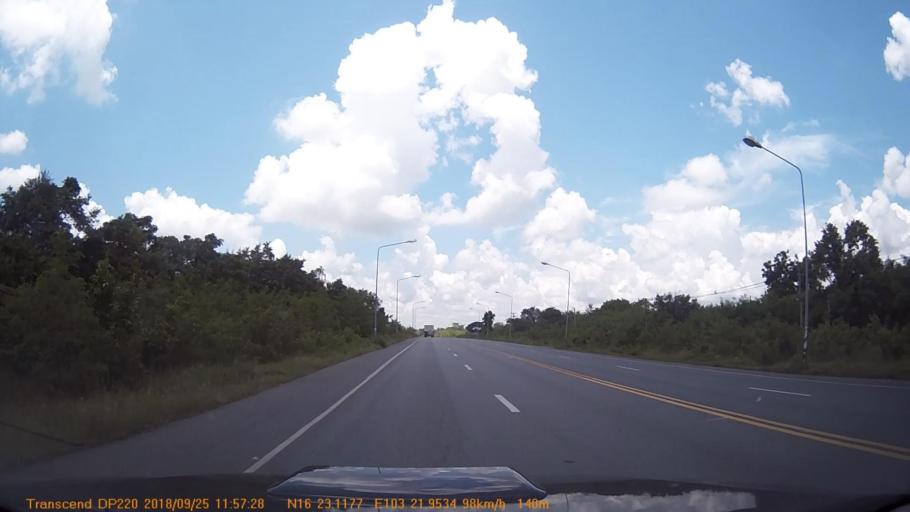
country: TH
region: Kalasin
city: Yang Talat
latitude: 16.3852
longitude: 103.3660
